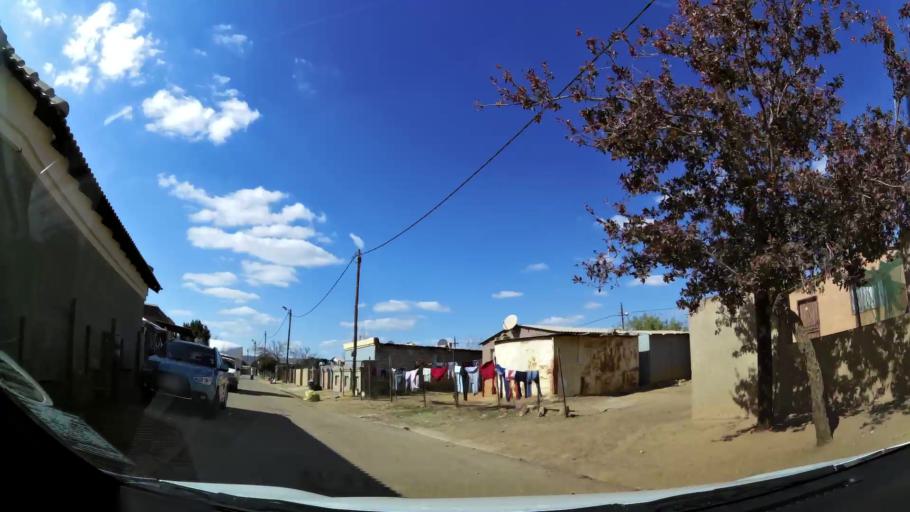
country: ZA
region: Gauteng
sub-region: City of Tshwane Metropolitan Municipality
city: Cullinan
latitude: -25.7230
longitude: 28.4041
